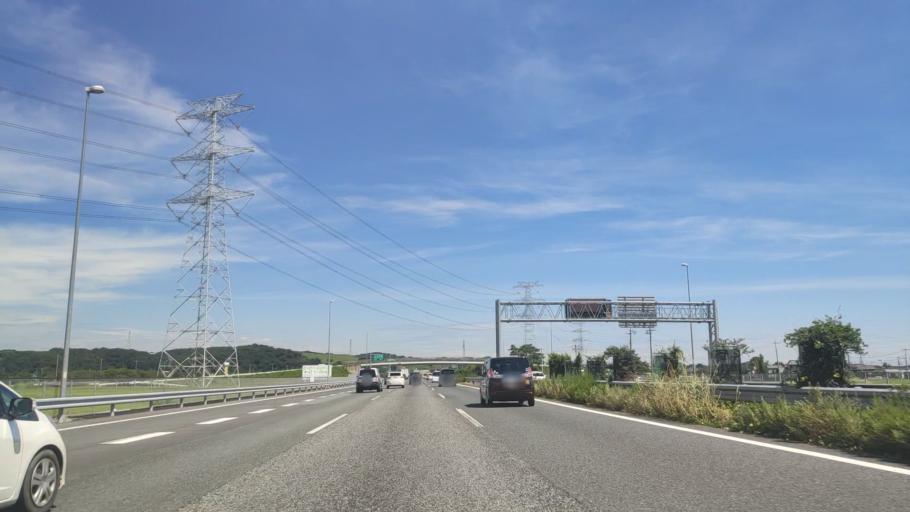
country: JP
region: Saitama
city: Sakado
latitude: 35.9711
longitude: 139.3789
